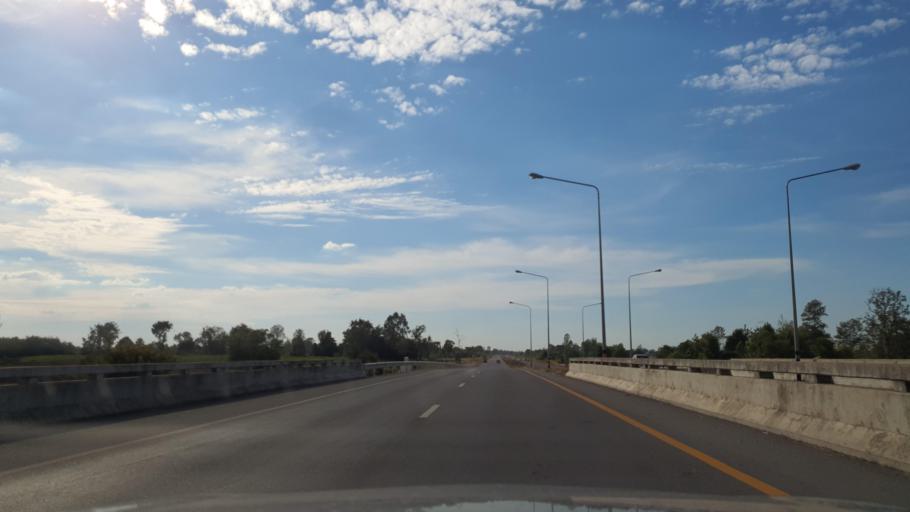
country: TH
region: Kalasin
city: Don Chan
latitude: 16.4117
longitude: 103.7573
